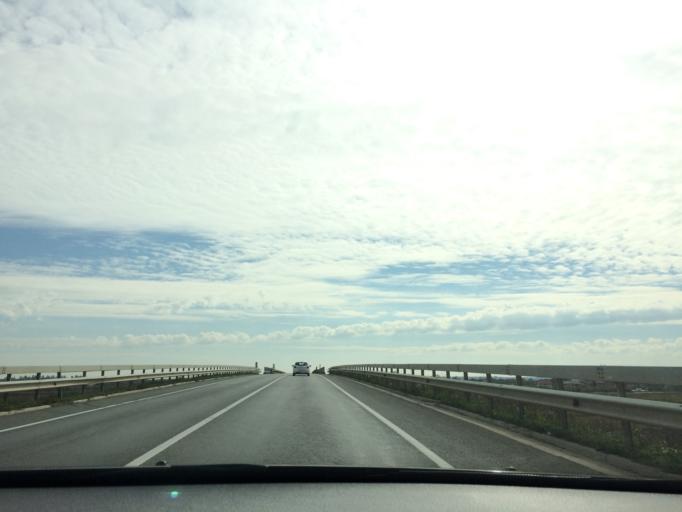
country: RO
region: Timis
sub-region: Comuna Ghiroda
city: Giarmata-Vii
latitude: 45.8097
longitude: 21.2950
